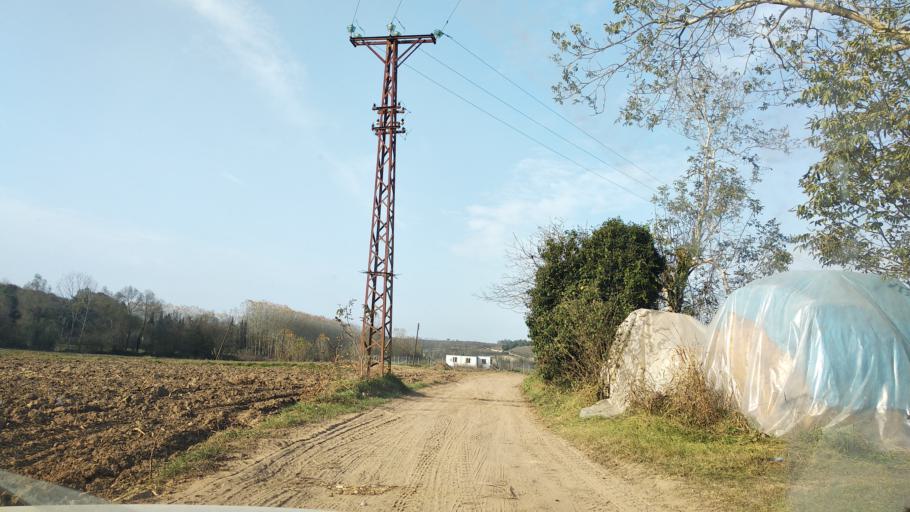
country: TR
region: Sakarya
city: Karasu
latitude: 41.0905
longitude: 30.5951
